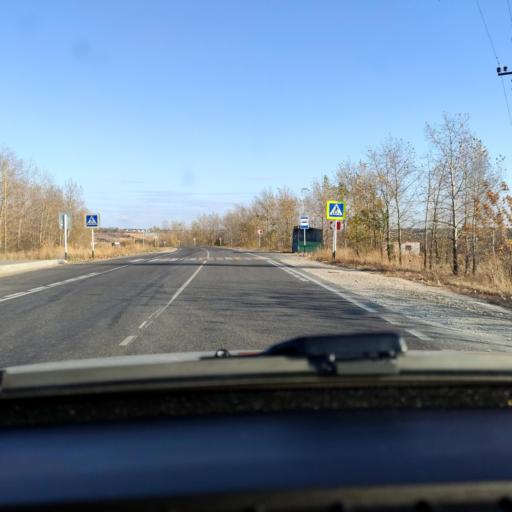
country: RU
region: Voronezj
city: Semiluki
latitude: 51.7233
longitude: 38.9945
